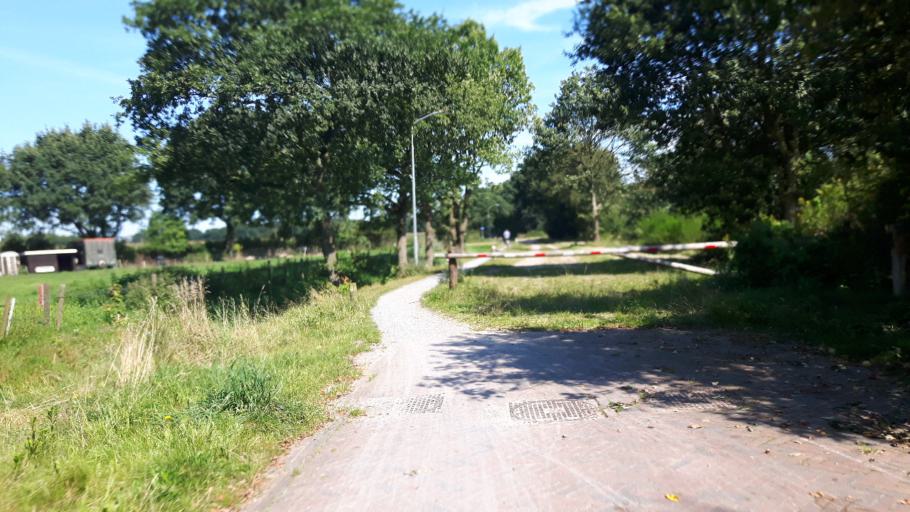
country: NL
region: Drenthe
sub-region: Gemeente Tynaarlo
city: Tynaarlo
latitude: 53.1185
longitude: 6.5947
